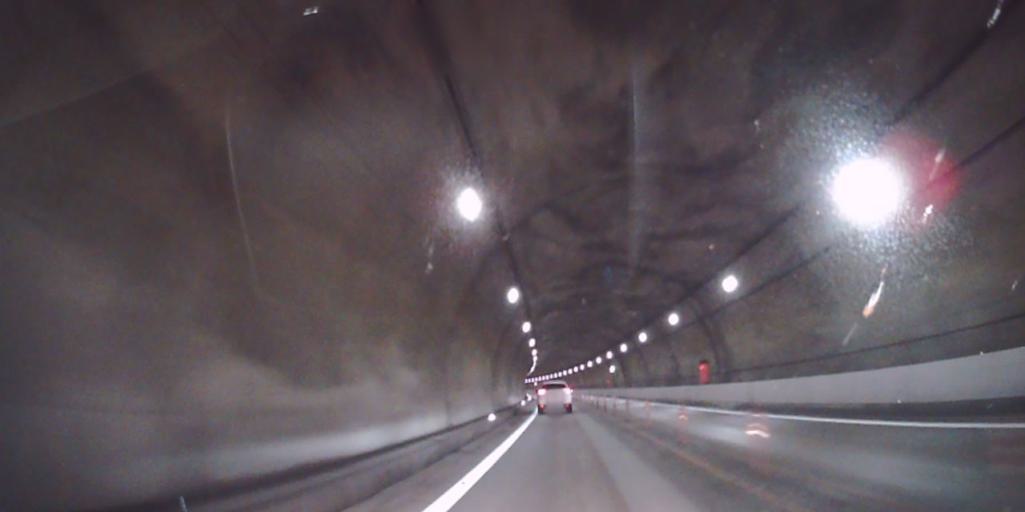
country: JP
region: Hokkaido
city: Date
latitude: 42.5894
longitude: 140.7204
